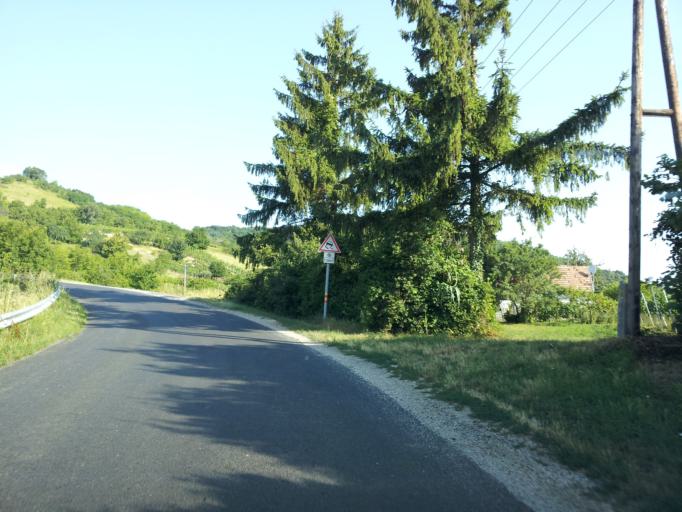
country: HU
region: Zala
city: Gyenesdias
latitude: 46.8562
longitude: 17.3403
